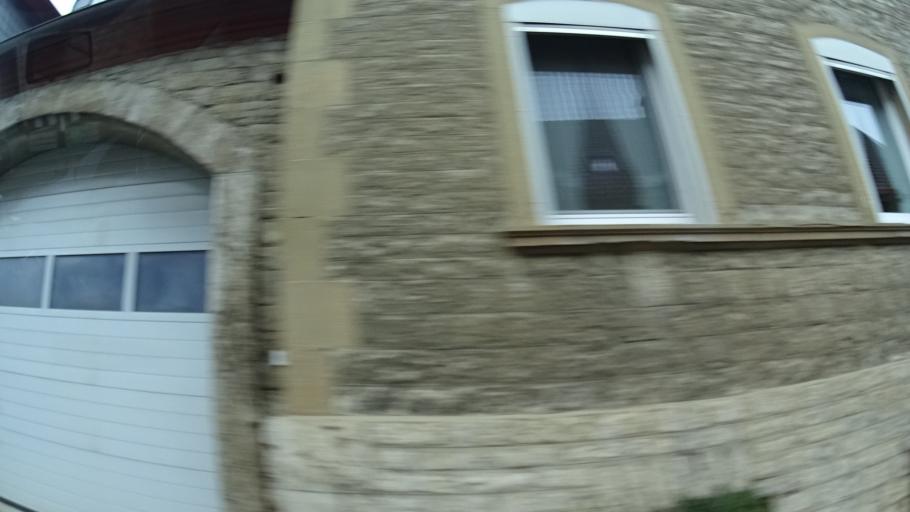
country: DE
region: Bavaria
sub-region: Regierungsbezirk Unterfranken
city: Segnitz
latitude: 49.6728
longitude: 10.1421
